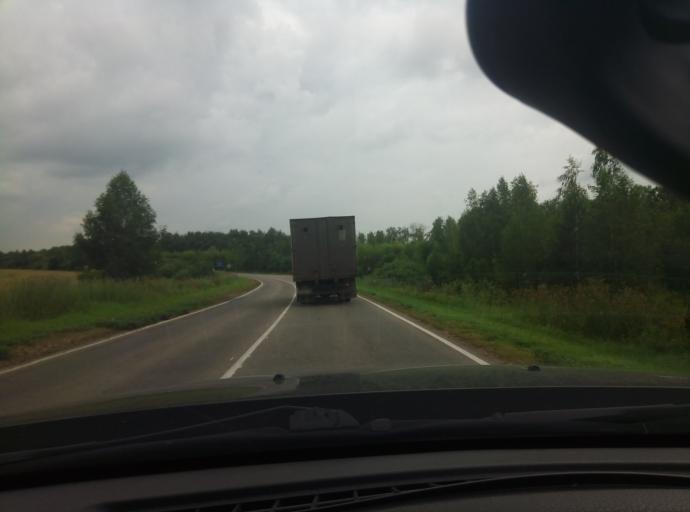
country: RU
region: Tula
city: Kimovsk
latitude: 53.9501
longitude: 38.5331
